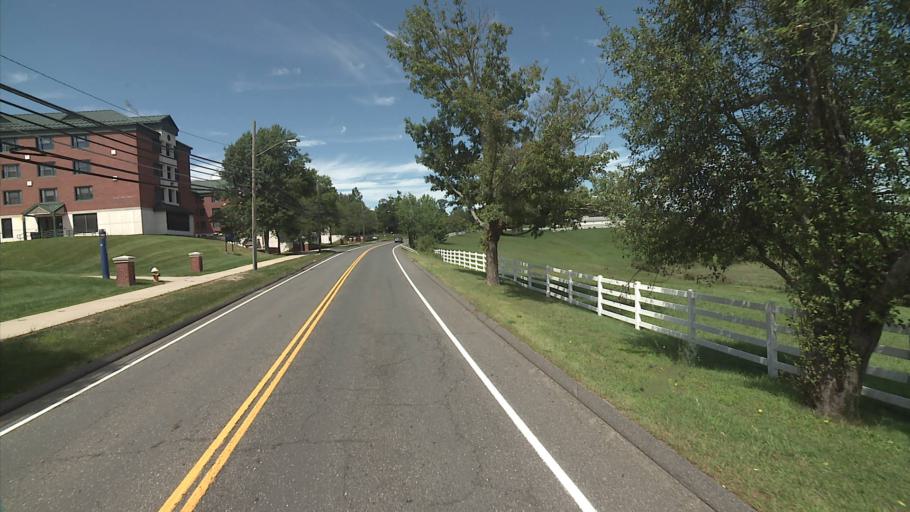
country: US
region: Connecticut
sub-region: Tolland County
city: Storrs
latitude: 41.8140
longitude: -72.2526
